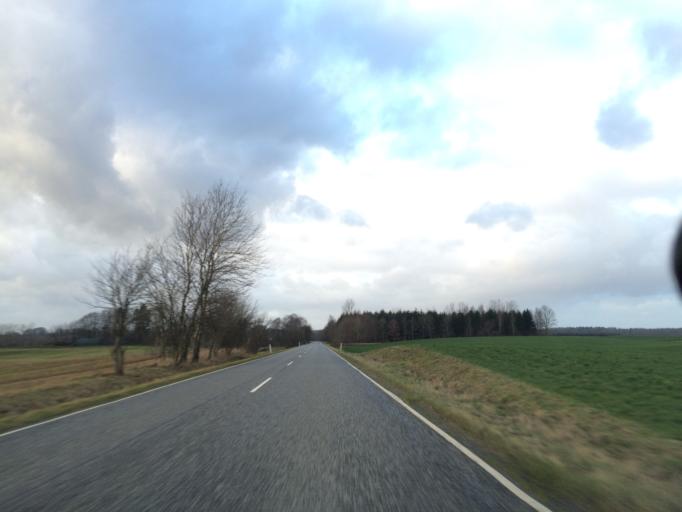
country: DK
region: Central Jutland
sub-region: Silkeborg Kommune
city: Svejbaek
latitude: 56.1017
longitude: 9.5994
